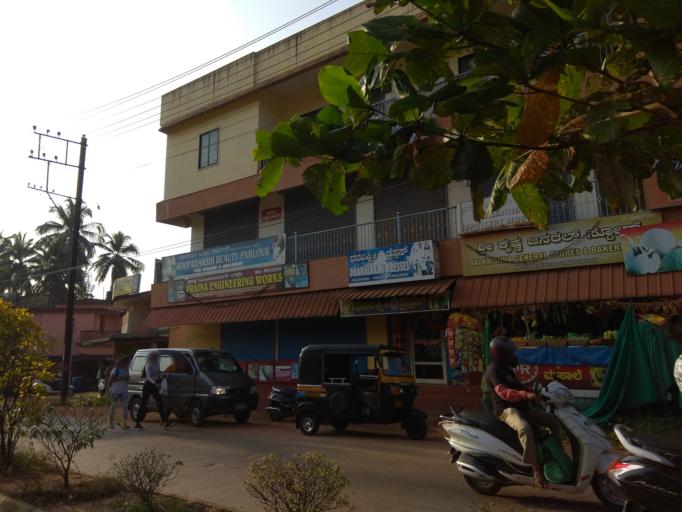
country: IN
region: Karnataka
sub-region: Dakshina Kannada
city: Mangalore
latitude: 12.9068
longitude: 74.8483
